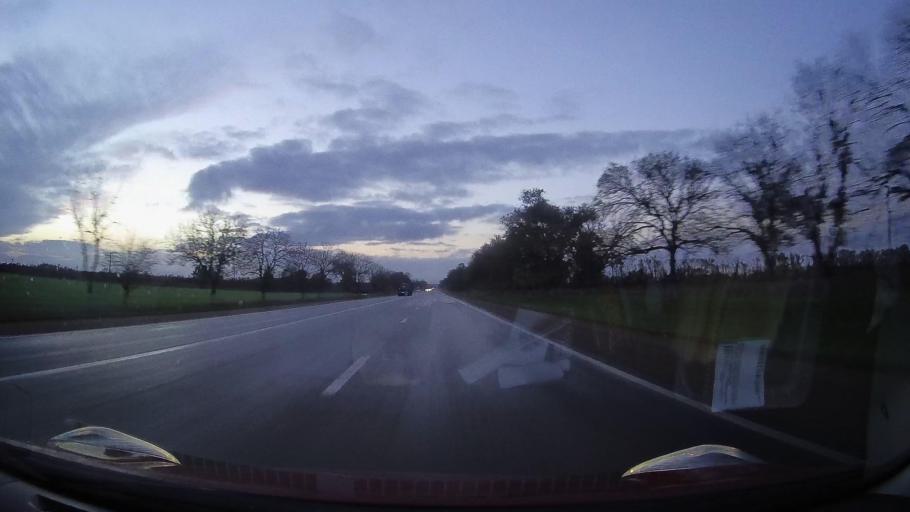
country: RU
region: Krasnodarskiy
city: Zavetnyy
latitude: 44.8956
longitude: 41.1959
